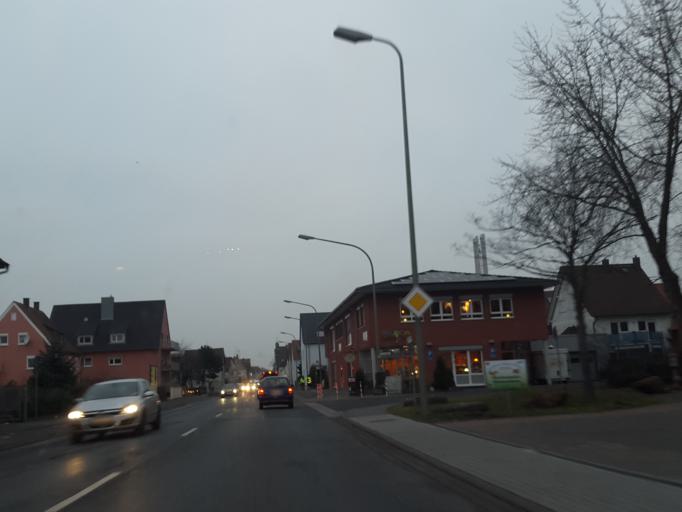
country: DE
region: Bavaria
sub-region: Regierungsbezirk Unterfranken
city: Kleinostheim
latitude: 49.9977
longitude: 9.0653
